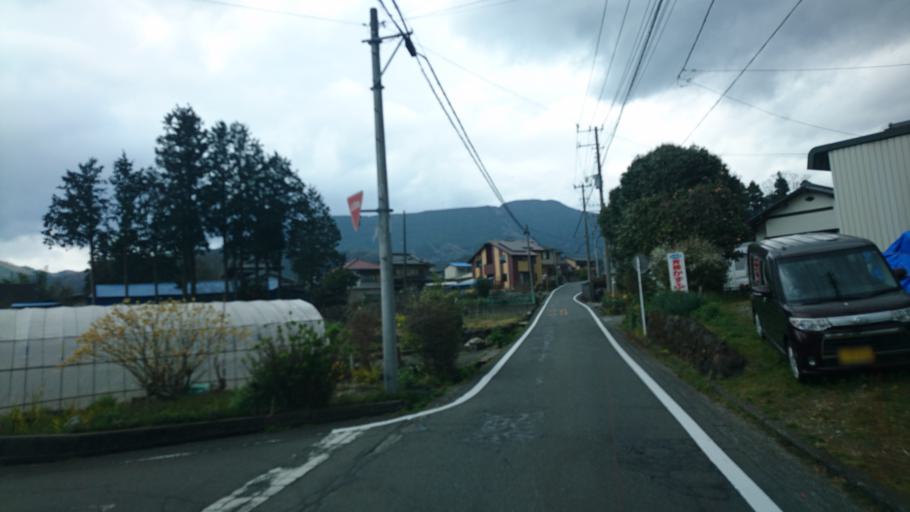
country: JP
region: Shizuoka
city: Fujinomiya
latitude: 35.2825
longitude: 138.5783
